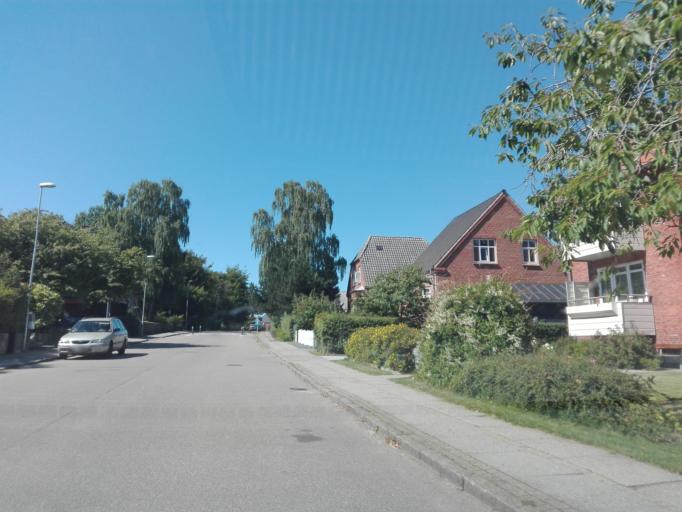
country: DK
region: Central Jutland
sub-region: Odder Kommune
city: Odder
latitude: 55.9704
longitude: 10.1581
